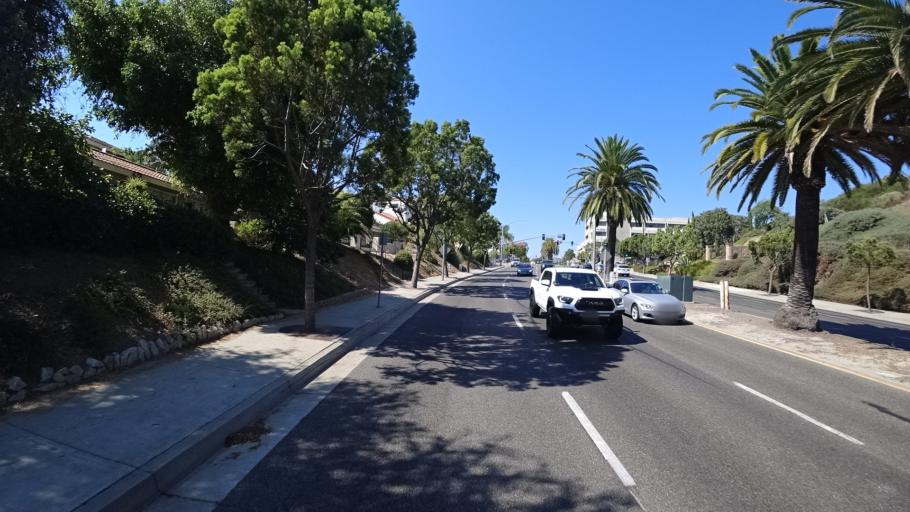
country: US
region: California
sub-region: Orange County
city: San Clemente
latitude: 33.4566
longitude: -117.6459
